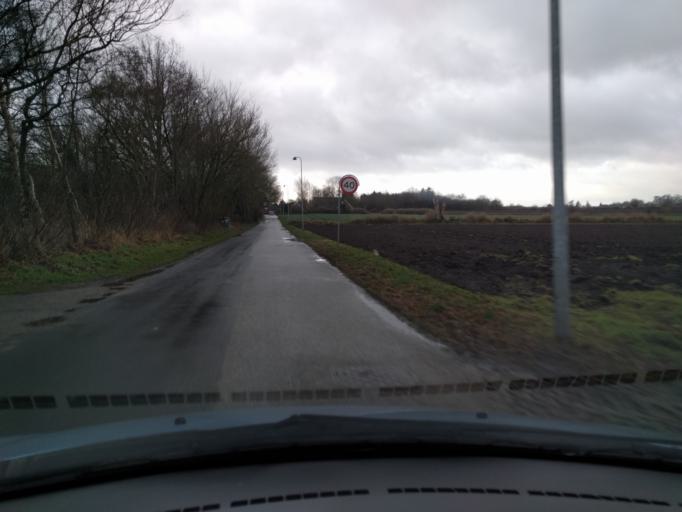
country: DK
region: South Denmark
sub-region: Kerteminde Kommune
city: Langeskov
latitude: 55.3422
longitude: 10.5440
